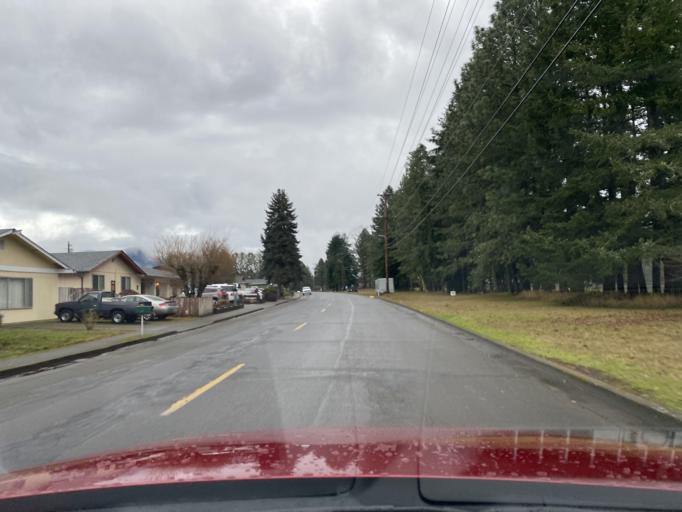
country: US
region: Oregon
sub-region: Lane County
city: Oakridge
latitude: 43.7485
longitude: -122.4808
